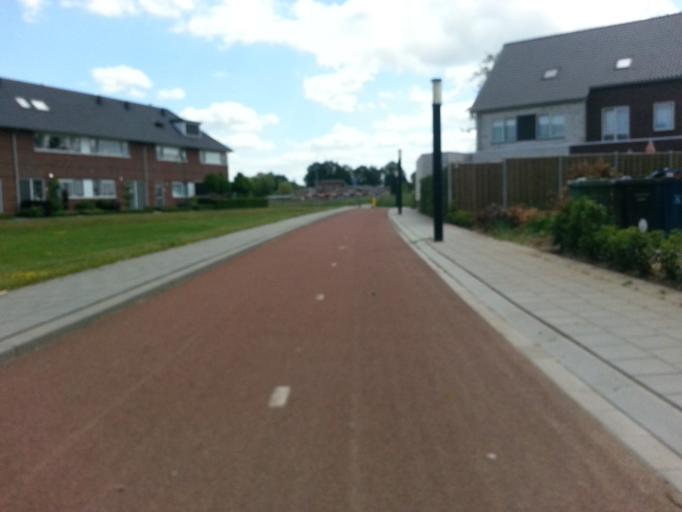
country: NL
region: Gelderland
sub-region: Gemeente Barneveld
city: Barneveld
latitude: 52.1279
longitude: 5.5801
